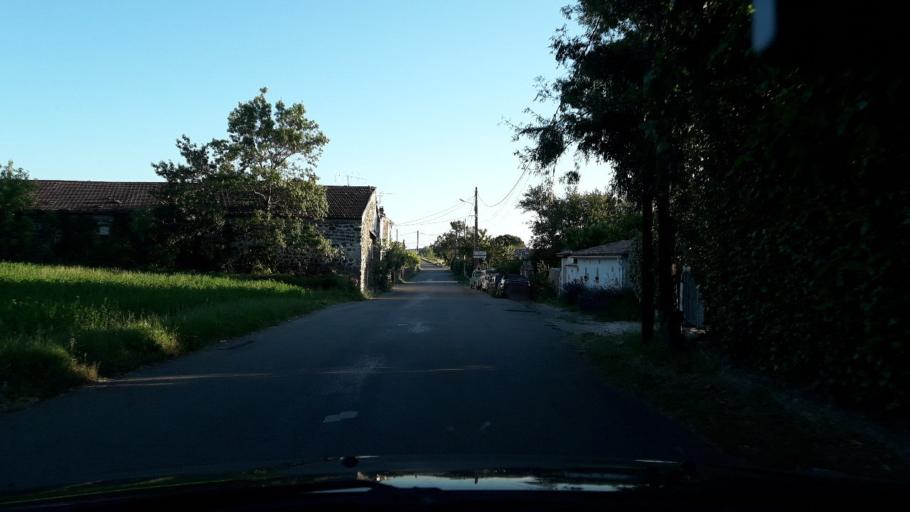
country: FR
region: Rhone-Alpes
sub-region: Departement de l'Ardeche
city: Lavilledieu
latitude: 44.6071
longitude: 4.4711
